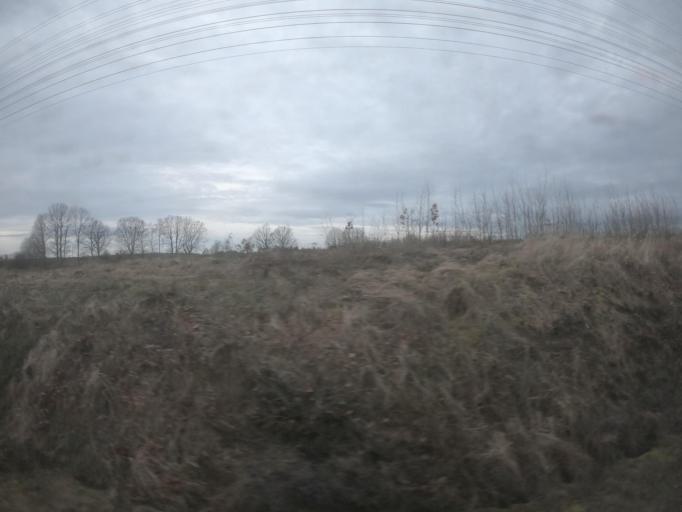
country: PL
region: West Pomeranian Voivodeship
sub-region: Powiat szczecinecki
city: Borne Sulinowo
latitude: 53.6295
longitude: 16.4807
